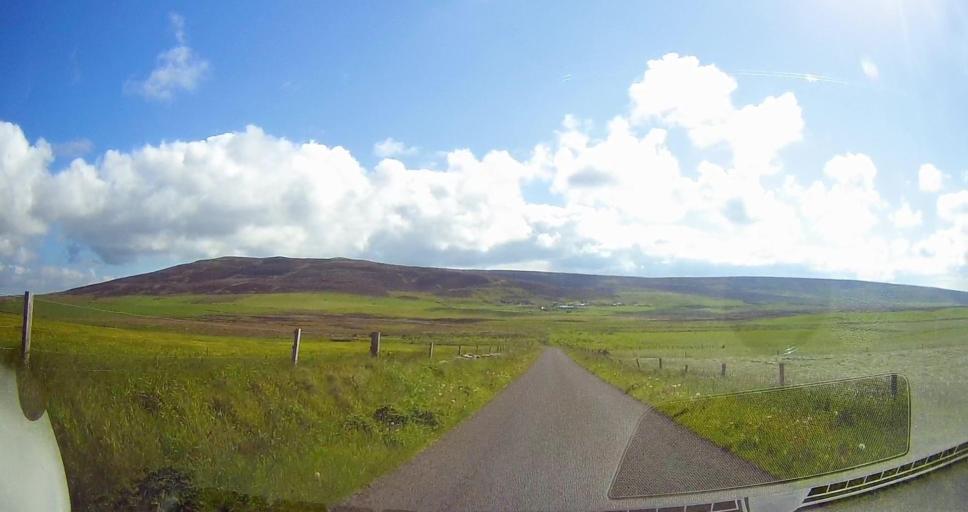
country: GB
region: Scotland
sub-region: Orkney Islands
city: Stromness
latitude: 58.9865
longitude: -3.1464
